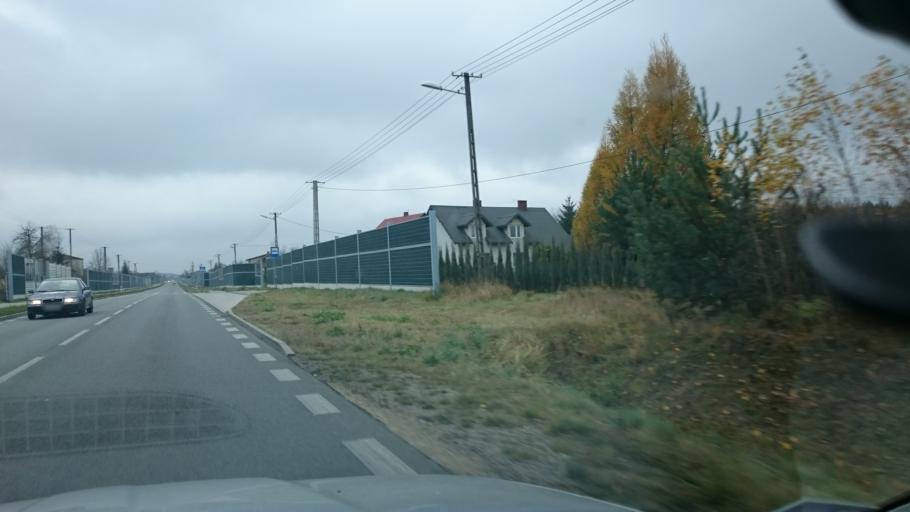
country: PL
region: Swietokrzyskie
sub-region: Powiat konecki
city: Konskie
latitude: 51.1679
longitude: 20.3788
